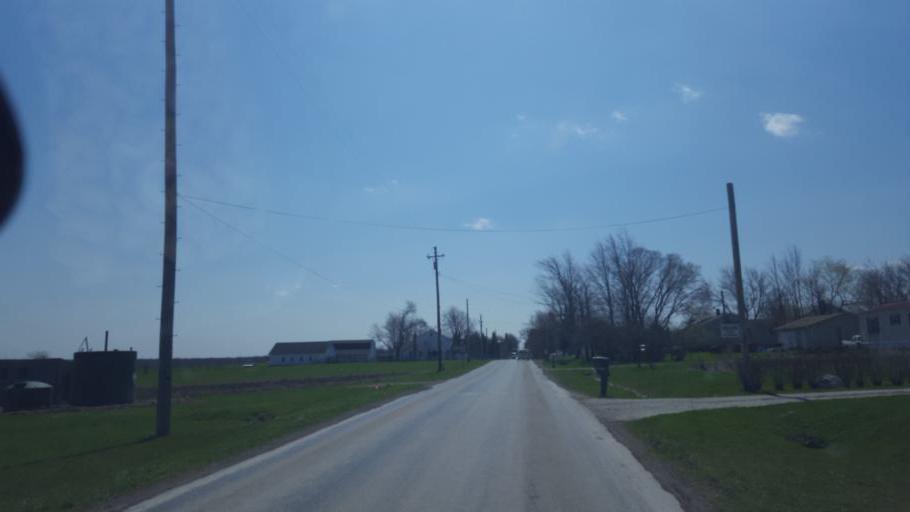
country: US
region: Ohio
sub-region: Geauga County
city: Middlefield
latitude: 41.4369
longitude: -81.0806
